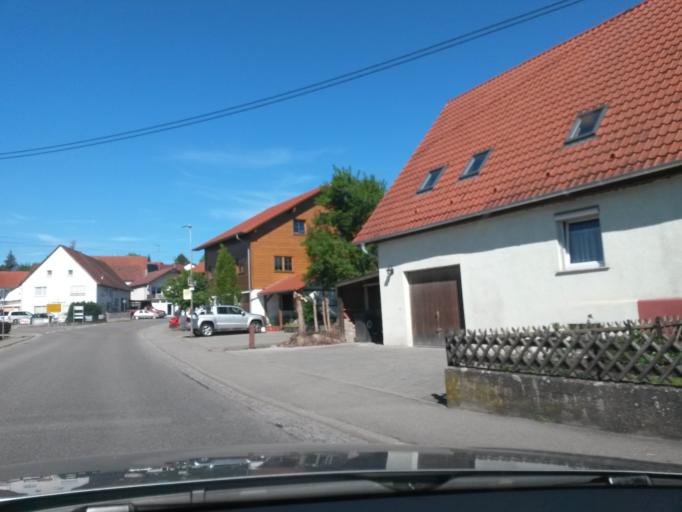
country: DE
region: Baden-Wuerttemberg
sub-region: Tuebingen Region
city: Kanzach
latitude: 48.0769
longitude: 9.5588
